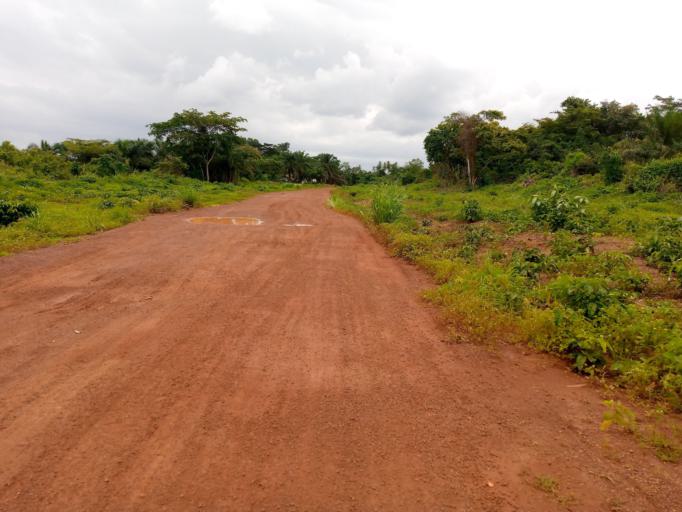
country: SL
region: Southern Province
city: Moyamba
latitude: 8.0846
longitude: -12.4504
